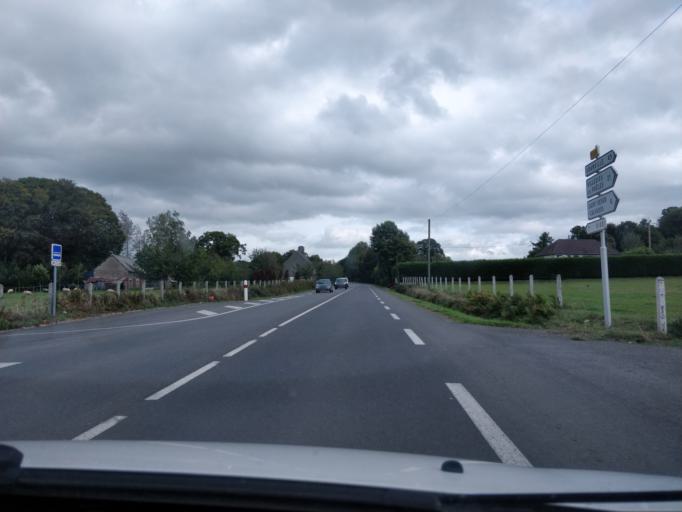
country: FR
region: Lower Normandy
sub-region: Departement du Calvados
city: Vire
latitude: 48.8398
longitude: -0.9629
